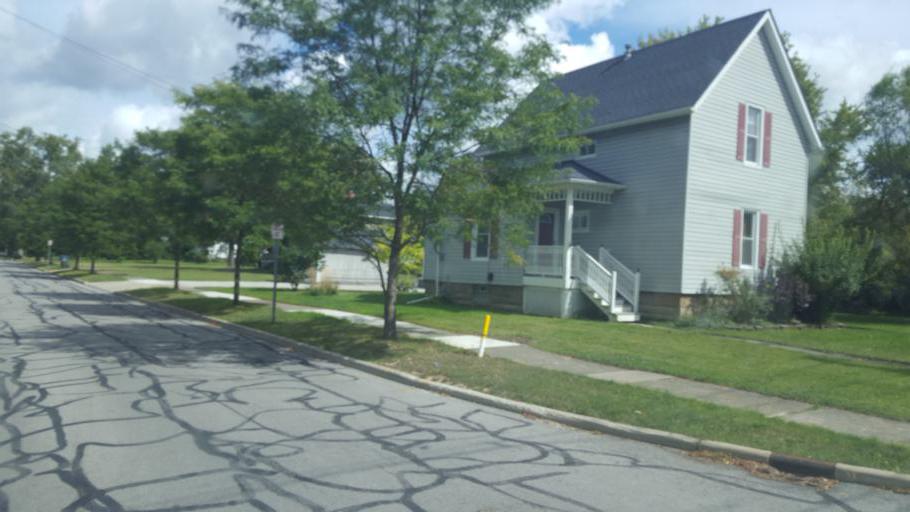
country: US
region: Ohio
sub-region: Lorain County
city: Oberlin
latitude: 41.2916
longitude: -82.2042
